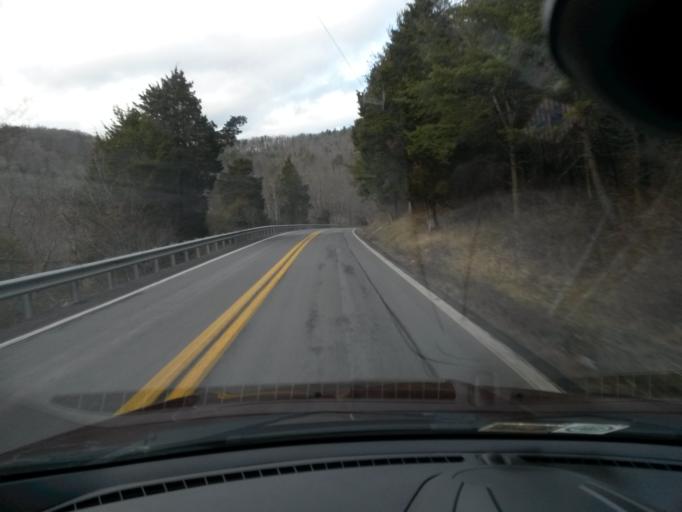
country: US
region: West Virginia
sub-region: Monroe County
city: Union
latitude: 37.5004
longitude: -80.6115
